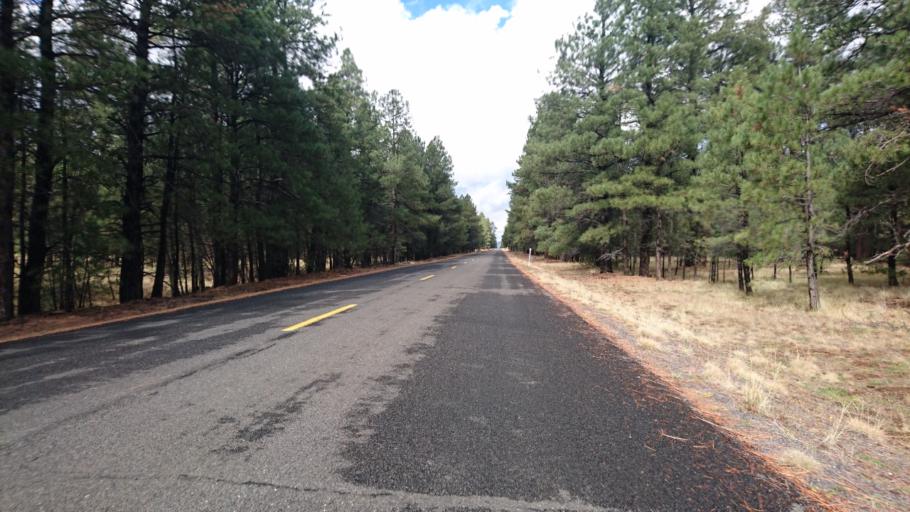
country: US
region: Arizona
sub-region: Coconino County
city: Parks
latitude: 35.2517
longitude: -111.8593
